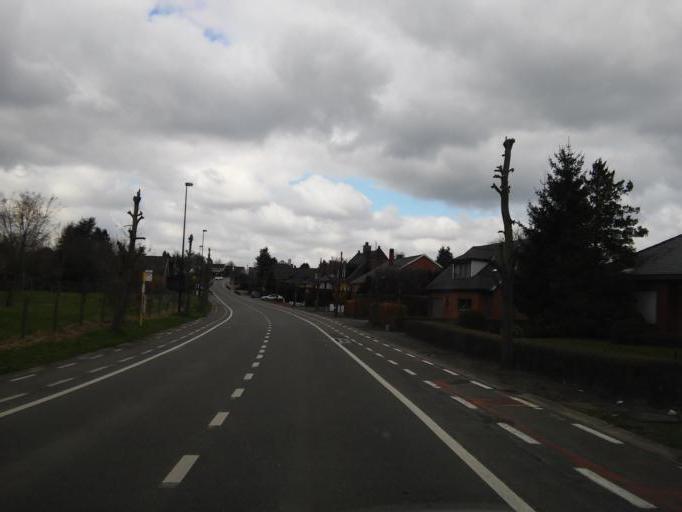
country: BE
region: Flanders
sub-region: Provincie Vlaams-Brabant
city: Sint-Pieters-Leeuw
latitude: 50.7846
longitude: 4.2466
